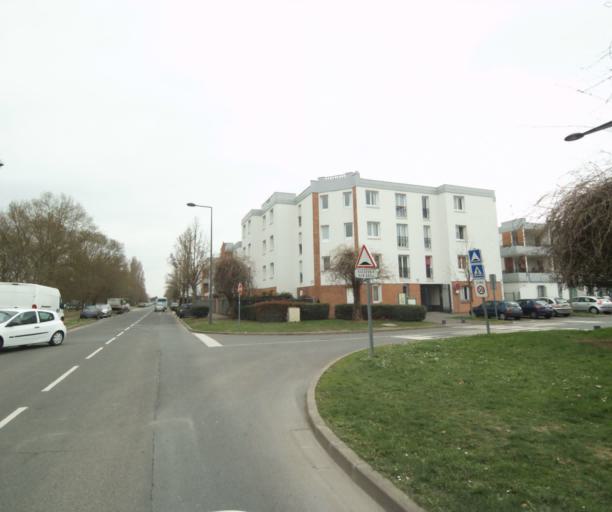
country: FR
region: Ile-de-France
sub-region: Departement du Val-d'Oise
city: Vaureal
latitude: 49.0508
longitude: 2.0399
